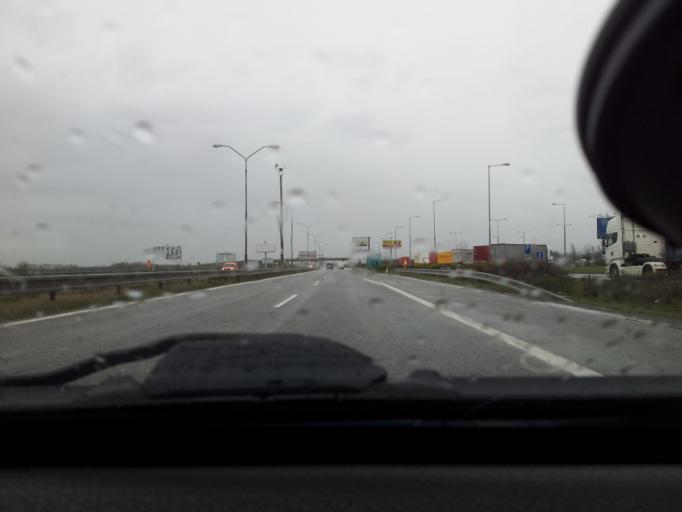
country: SK
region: Bratislavsky
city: Svaty Jur
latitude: 48.1885
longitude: 17.2068
